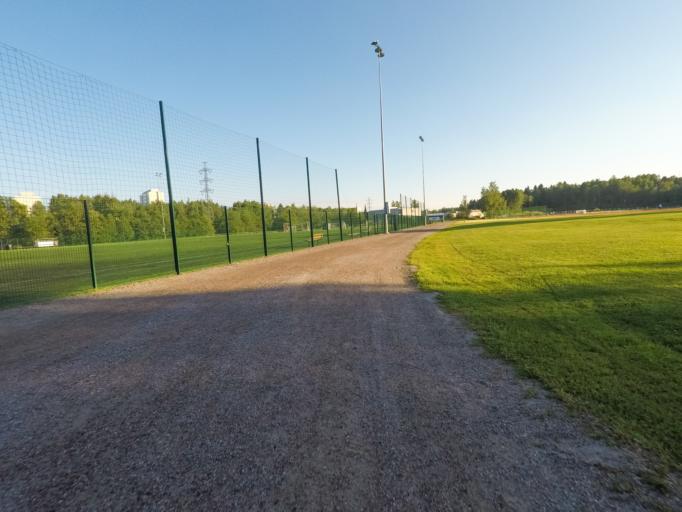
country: FI
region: Uusimaa
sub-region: Helsinki
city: Vantaa
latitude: 60.2176
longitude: 25.0763
